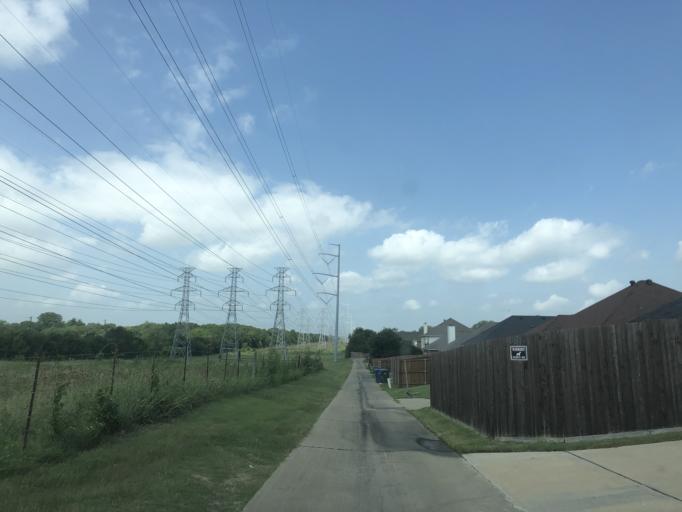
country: US
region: Texas
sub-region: Dallas County
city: Sunnyvale
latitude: 32.8344
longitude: -96.5655
